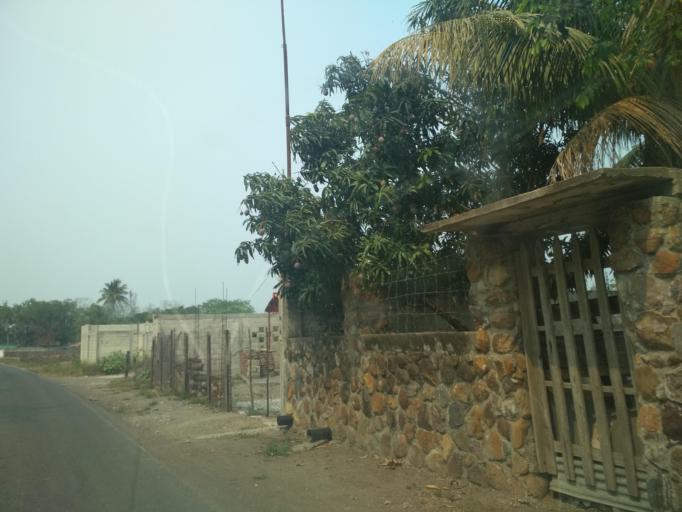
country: MX
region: Veracruz
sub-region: Veracruz
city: Delfino Victoria (Santa Fe)
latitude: 19.2106
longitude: -96.3169
